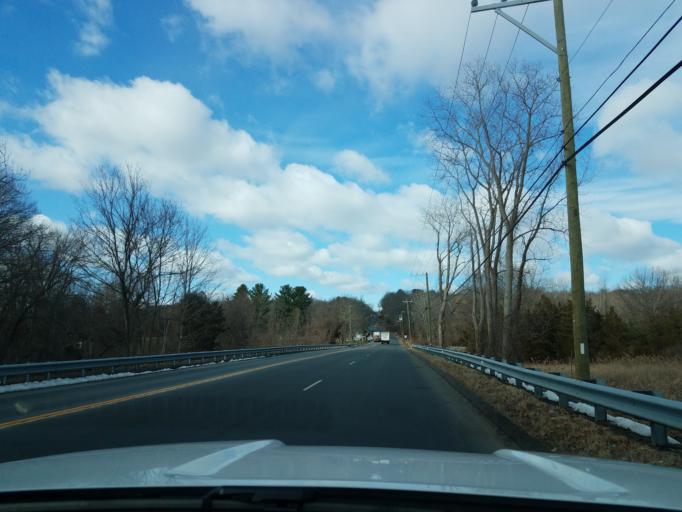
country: US
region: Connecticut
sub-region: Hartford County
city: Plainville
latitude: 41.6407
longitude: -72.8799
